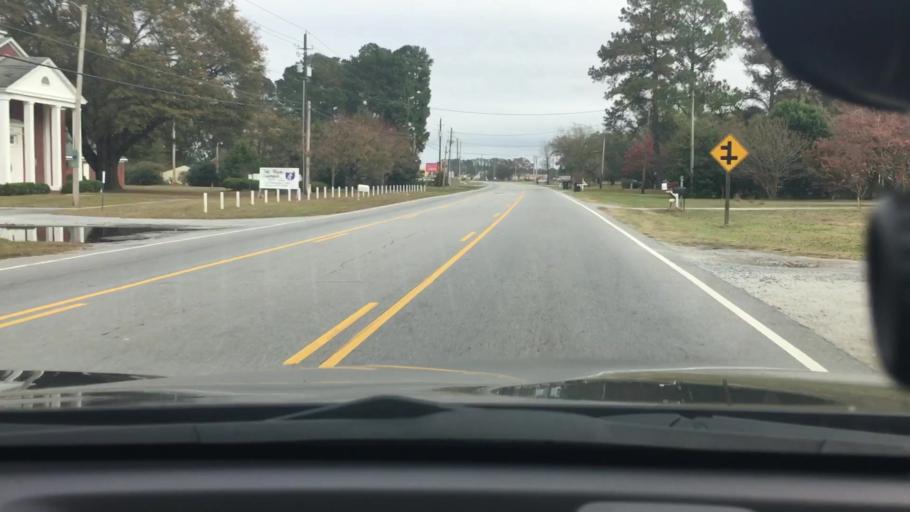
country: US
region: North Carolina
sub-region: Pitt County
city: Greenville
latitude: 35.6263
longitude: -77.3375
